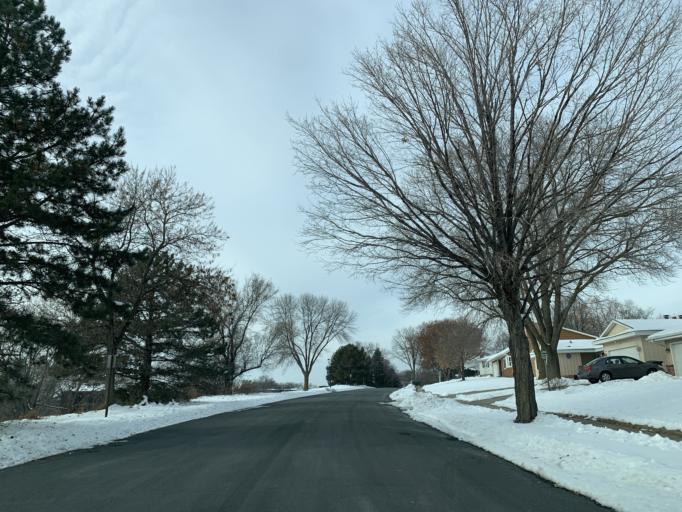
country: US
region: Minnesota
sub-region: Scott County
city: Savage
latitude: 44.8205
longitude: -93.3439
